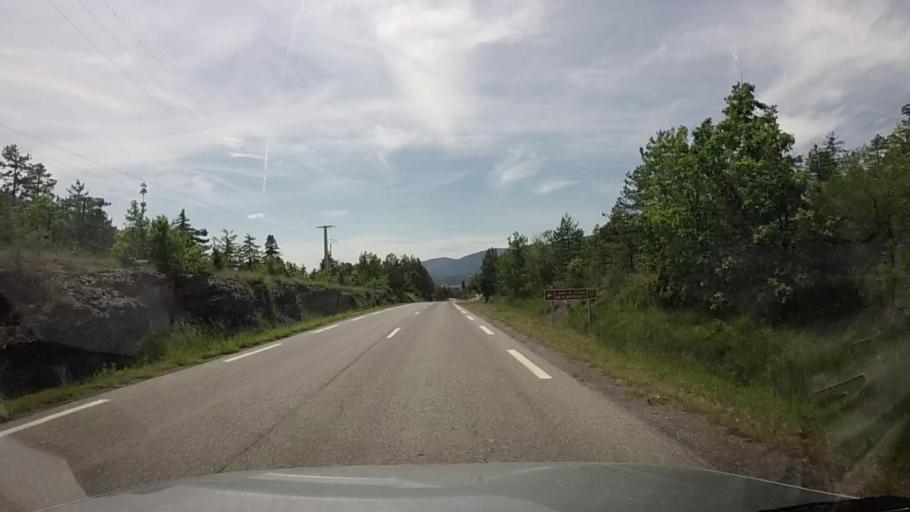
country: FR
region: Provence-Alpes-Cote d'Azur
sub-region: Departement des Alpes-de-Haute-Provence
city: Le Brusquet
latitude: 44.1646
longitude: 6.3217
